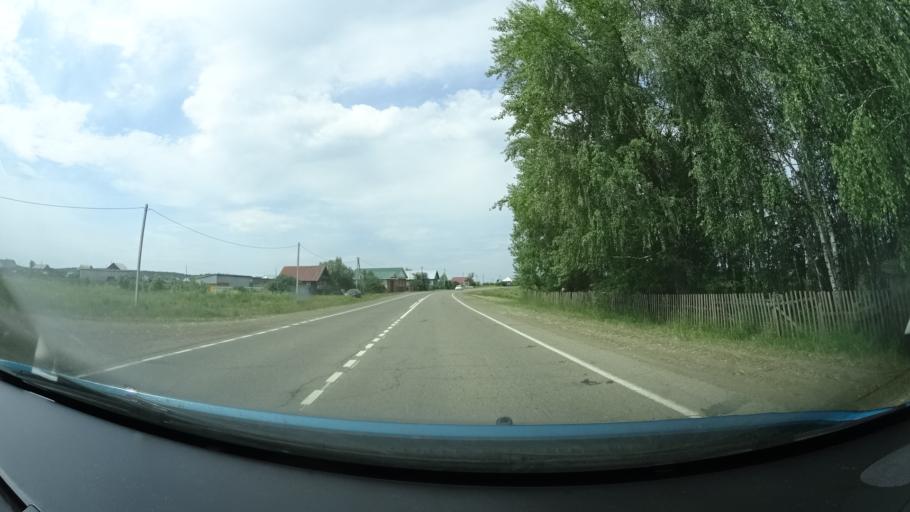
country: RU
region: Perm
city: Barda
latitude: 56.8386
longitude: 55.6147
